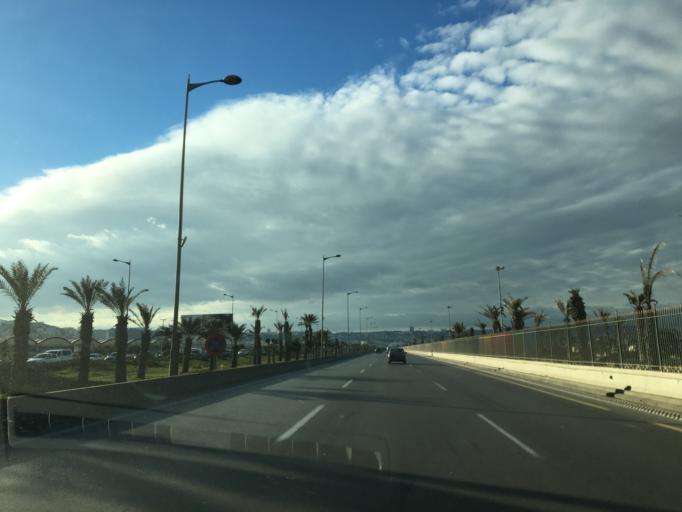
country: DZ
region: Alger
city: Bab Ezzouar
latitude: 36.7419
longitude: 3.1177
